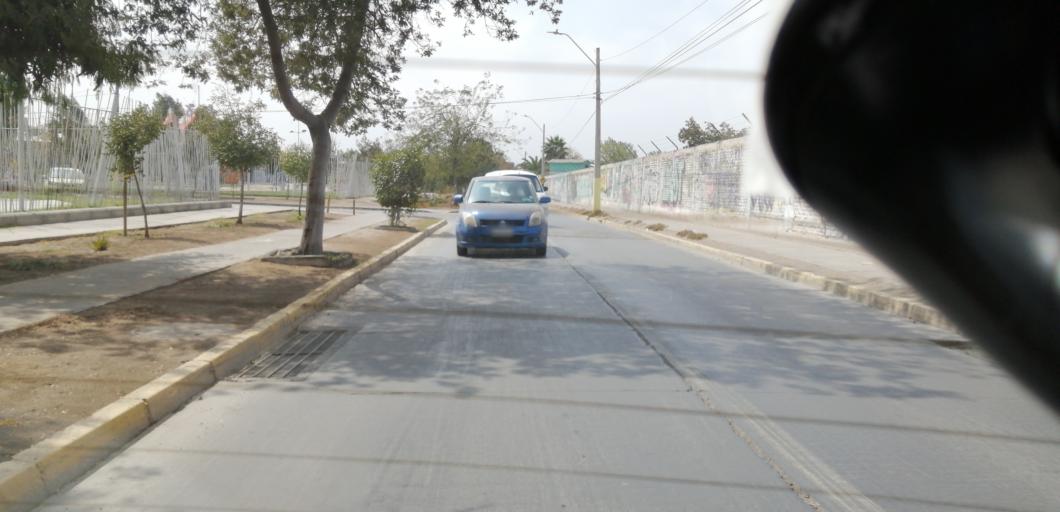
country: CL
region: Santiago Metropolitan
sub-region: Provincia de Santiago
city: Lo Prado
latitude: -33.4421
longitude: -70.7472
